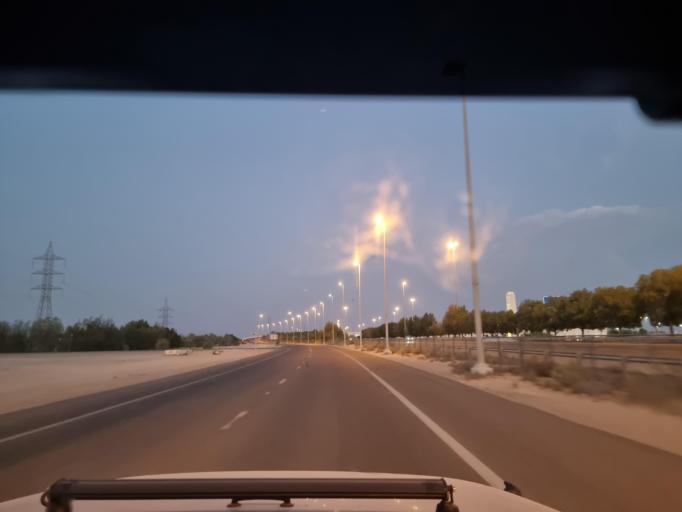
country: AE
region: Abu Dhabi
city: Abu Dhabi
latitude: 24.1913
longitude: 54.9961
